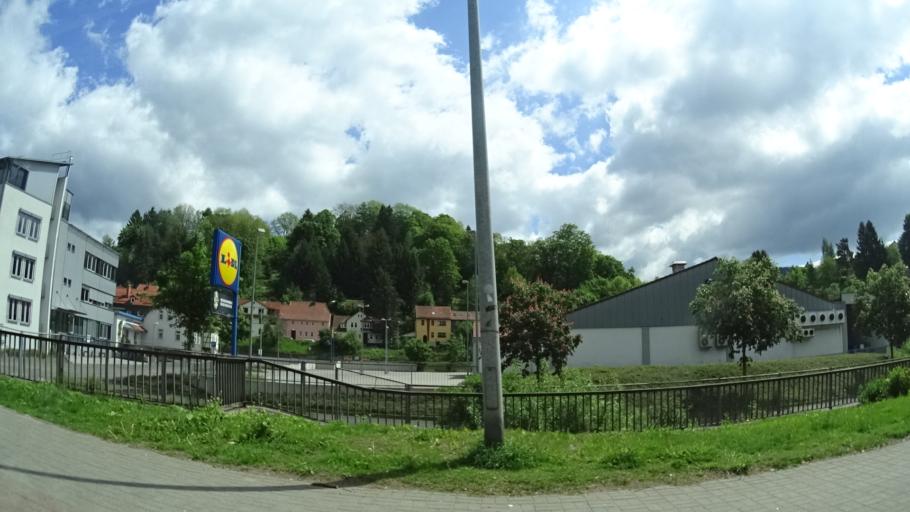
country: DE
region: Thuringia
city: Suhl
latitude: 50.6157
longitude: 10.6977
